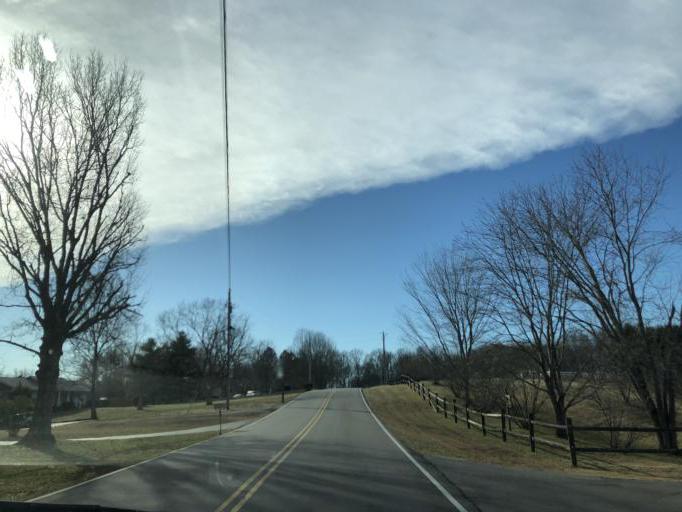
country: US
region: Tennessee
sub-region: Wilson County
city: Mount Juliet
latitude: 36.1616
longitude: -86.5605
